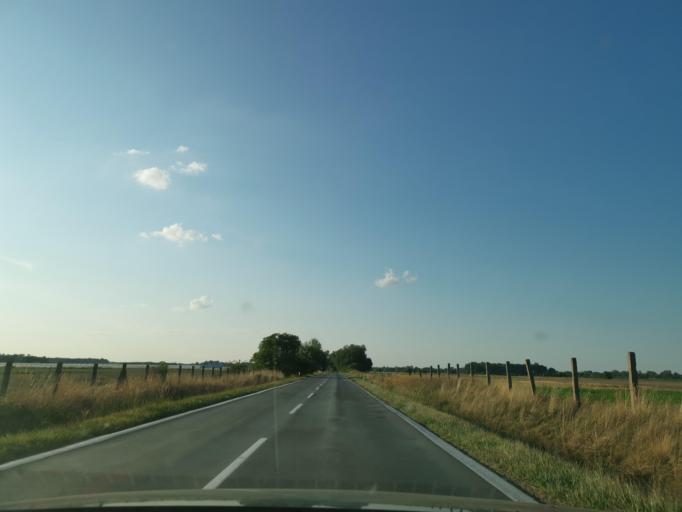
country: SK
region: Bratislavsky
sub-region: Okres Malacky
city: Malacky
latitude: 48.5129
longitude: 16.9948
